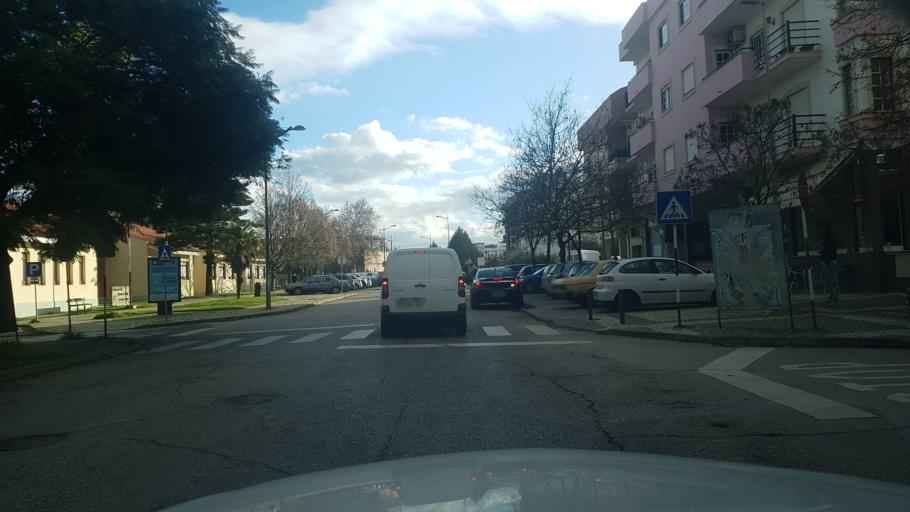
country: PT
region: Santarem
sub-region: Entroncamento
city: Entroncamento
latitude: 39.4666
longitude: -8.4719
